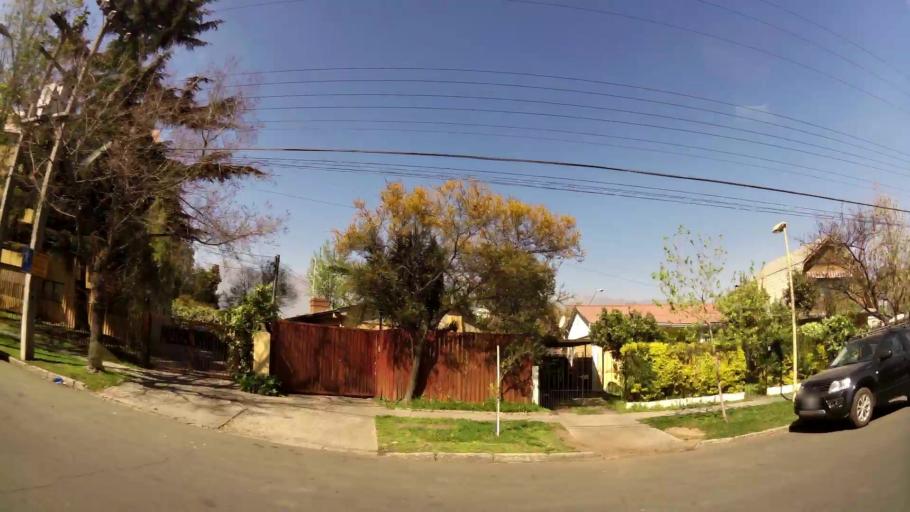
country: CL
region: Santiago Metropolitan
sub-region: Provincia de Santiago
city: Villa Presidente Frei, Nunoa, Santiago, Chile
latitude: -33.4280
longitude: -70.5694
